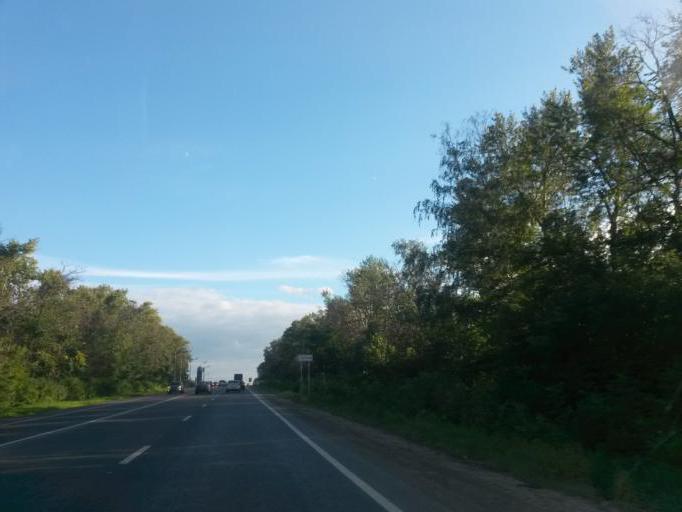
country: RU
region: Moskovskaya
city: Gorki-Leninskiye
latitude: 55.5144
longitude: 37.7583
